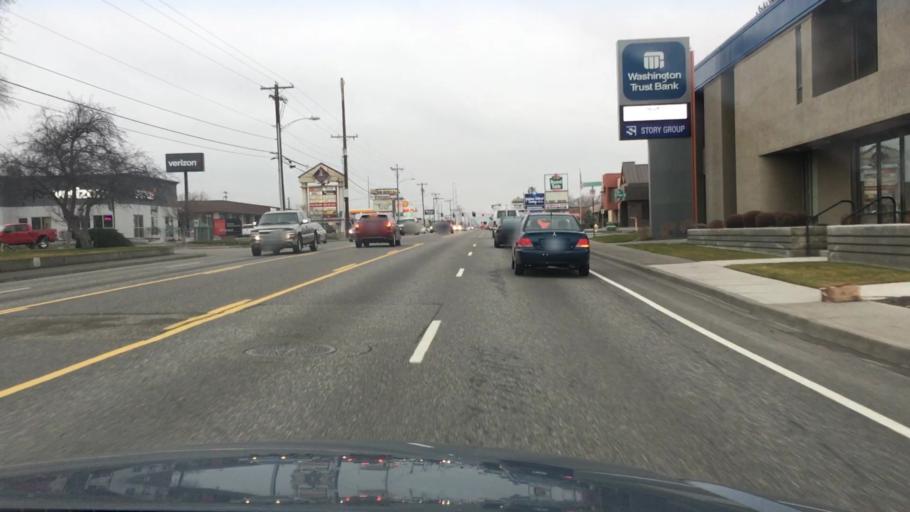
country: US
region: Washington
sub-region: Benton County
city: Kennewick
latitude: 46.2124
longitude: -119.1652
